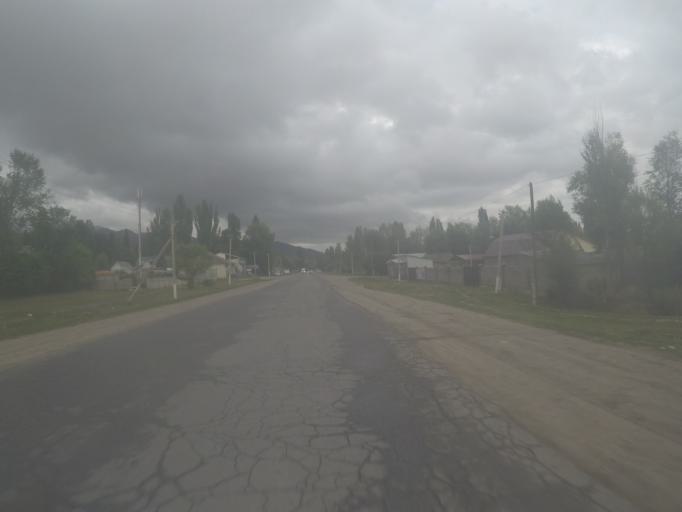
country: KG
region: Ysyk-Koel
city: Tyup
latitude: 42.7818
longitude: 78.2900
